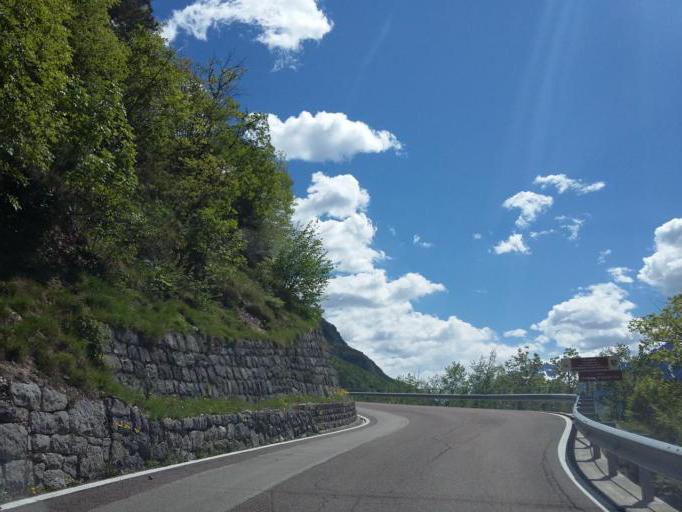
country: IT
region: Trentino-Alto Adige
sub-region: Provincia di Trento
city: Moscheri
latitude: 45.8250
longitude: 11.0854
